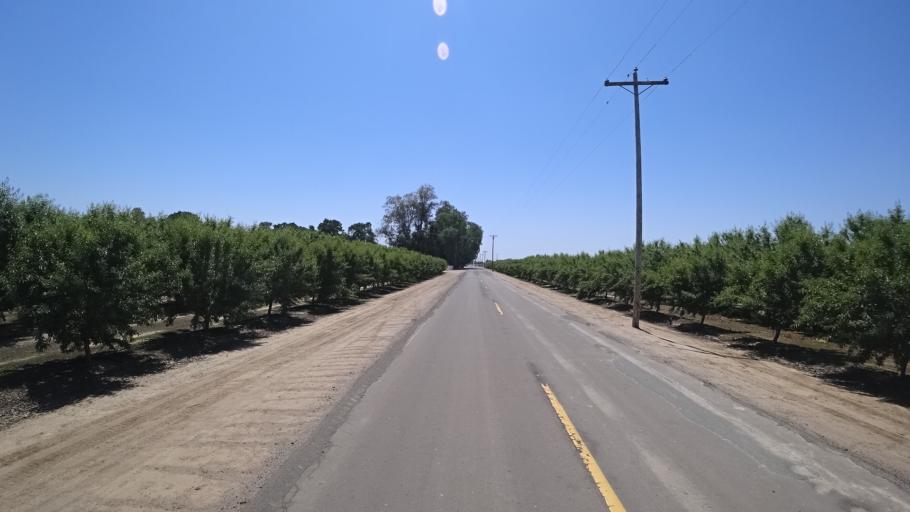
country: US
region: California
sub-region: Kings County
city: Lemoore
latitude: 36.2864
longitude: -119.7628
